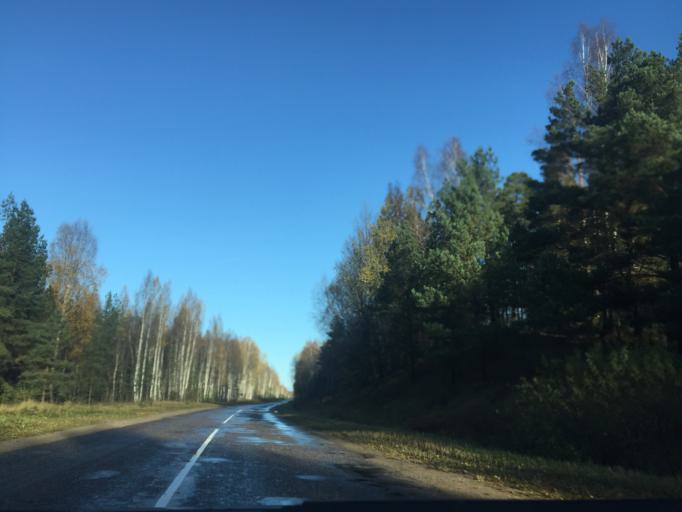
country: LV
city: Tireli
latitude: 56.8983
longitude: 23.5313
